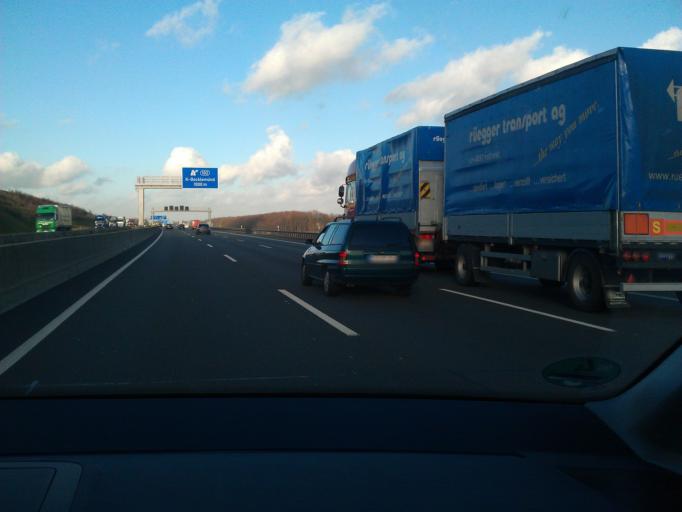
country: DE
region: North Rhine-Westphalia
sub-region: Regierungsbezirk Koln
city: Mengenich
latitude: 50.9626
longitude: 6.8508
